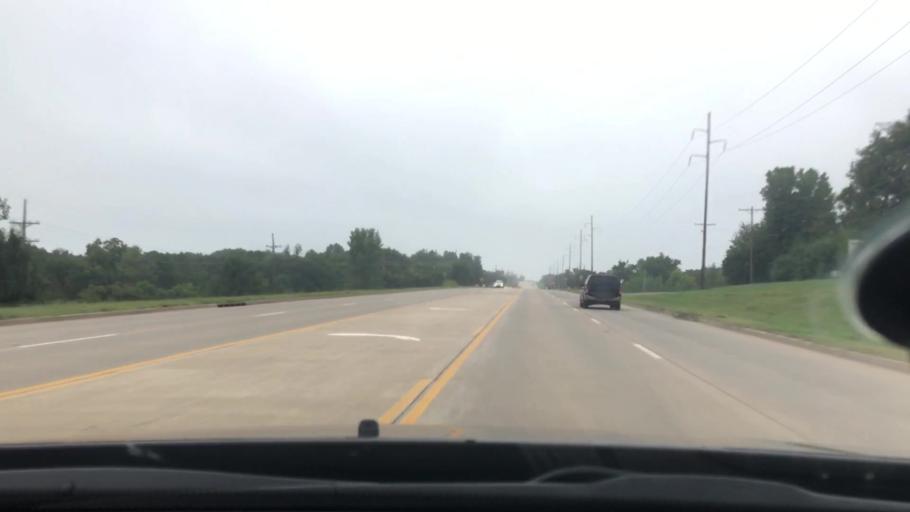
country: US
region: Oklahoma
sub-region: Seminole County
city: Seminole
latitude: 35.2522
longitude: -96.6709
